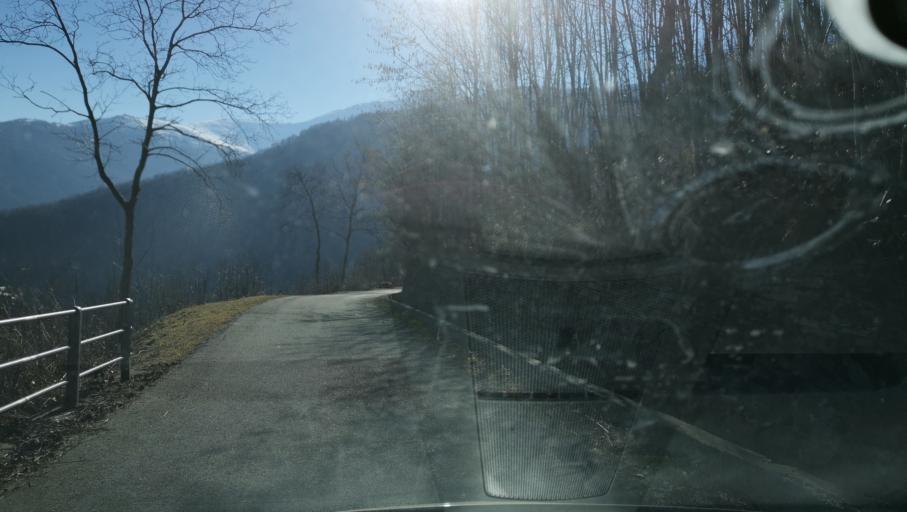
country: IT
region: Piedmont
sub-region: Provincia di Torino
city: Rora
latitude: 44.7918
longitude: 7.1945
